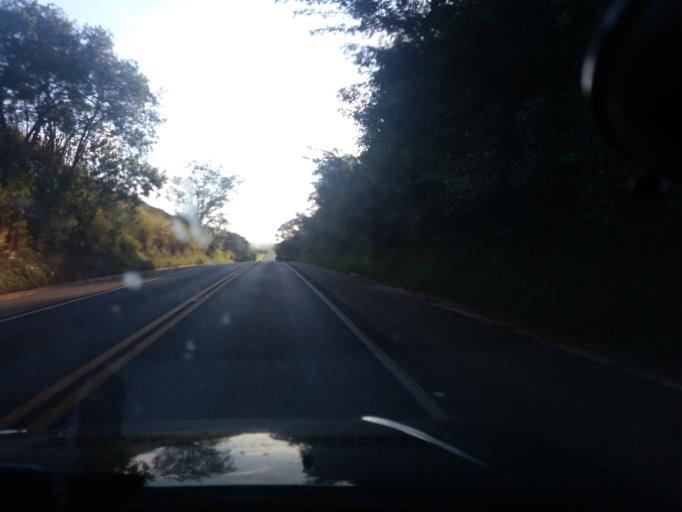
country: BR
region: Sao Paulo
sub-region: Buri
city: Buri
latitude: -23.9318
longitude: -48.6394
